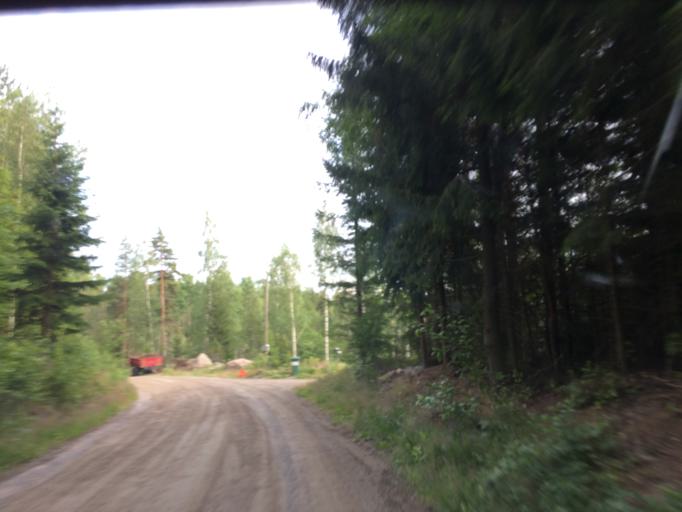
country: FI
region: Haeme
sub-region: Haemeenlinna
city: Janakkala
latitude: 60.8839
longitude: 24.6103
